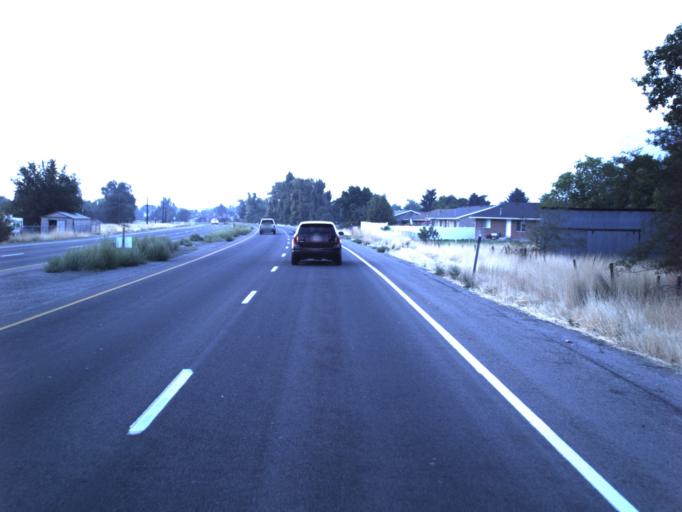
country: US
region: Utah
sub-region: Utah County
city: Springville
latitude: 40.1496
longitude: -111.6046
